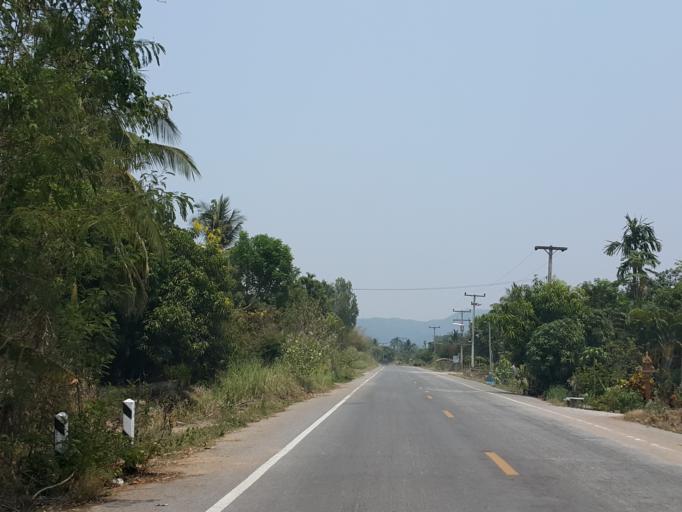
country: TH
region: Kamphaeng Phet
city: Pang Sila Thong
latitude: 16.0548
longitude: 99.3574
